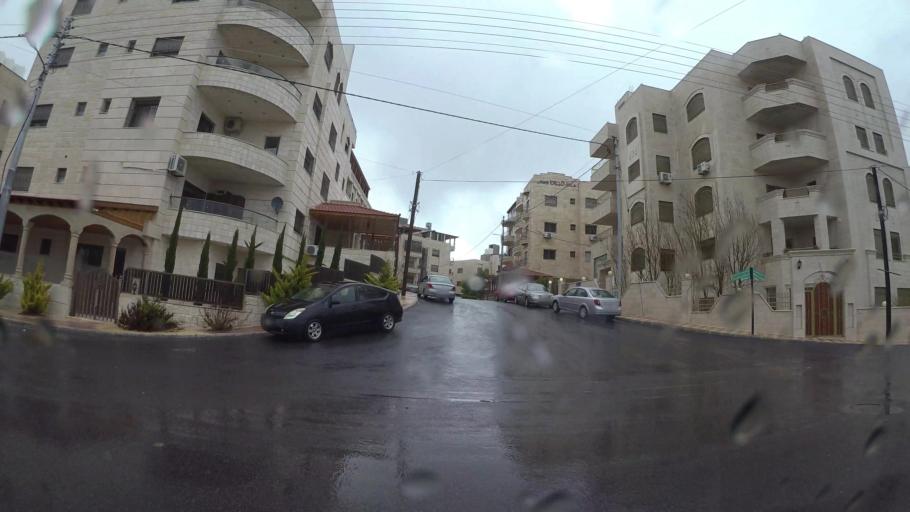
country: JO
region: Amman
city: Al Jubayhah
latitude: 32.0238
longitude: 35.8826
